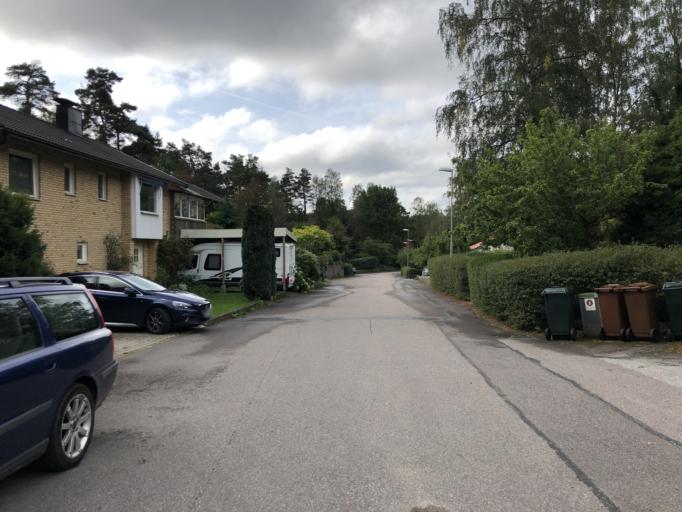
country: SE
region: Vaestra Goetaland
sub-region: Goteborg
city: Majorna
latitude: 57.7436
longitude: 11.9042
